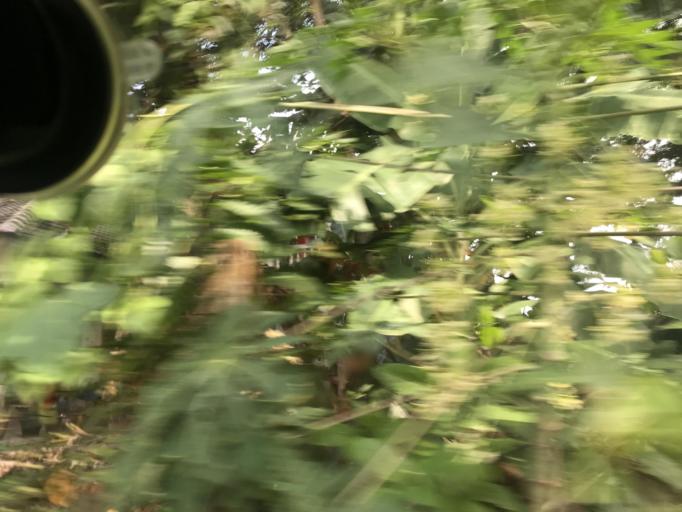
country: MY
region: Kelantan
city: Kota Bharu
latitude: 6.1129
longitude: 102.2371
